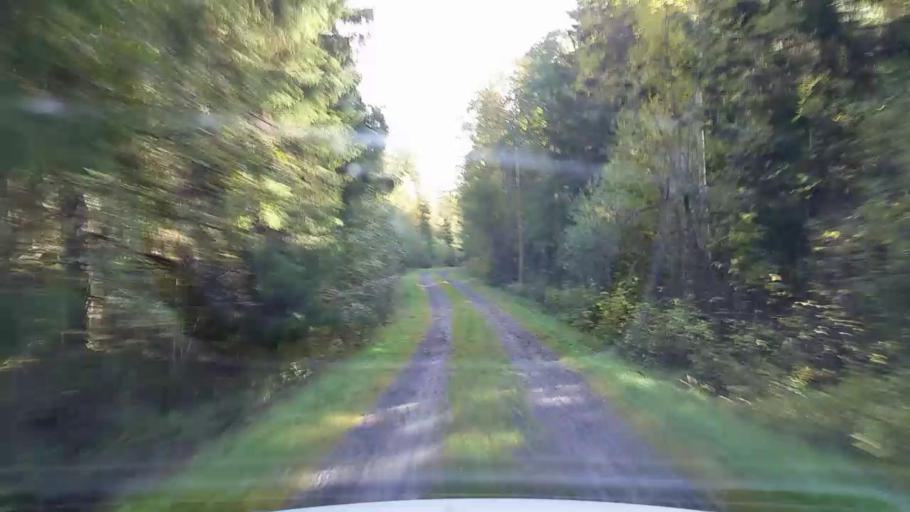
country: SE
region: Gaevleborg
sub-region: Ljusdals Kommun
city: Jaervsoe
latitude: 61.7805
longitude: 16.1796
